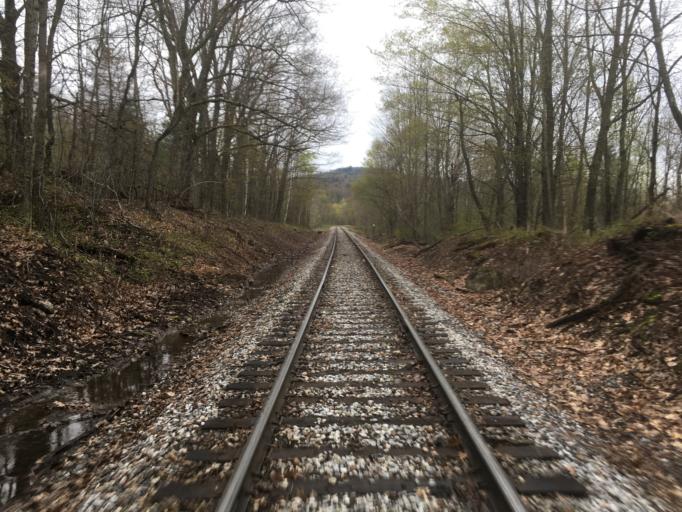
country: US
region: Vermont
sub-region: Rutland County
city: Rutland
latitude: 43.4789
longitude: -72.8751
